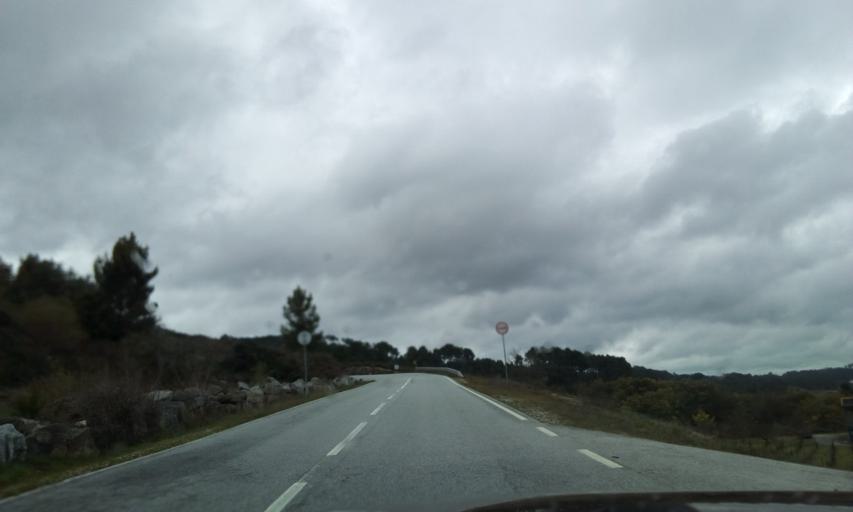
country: PT
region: Viseu
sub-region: Viseu
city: Rio de Loba
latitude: 40.6131
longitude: -7.8641
